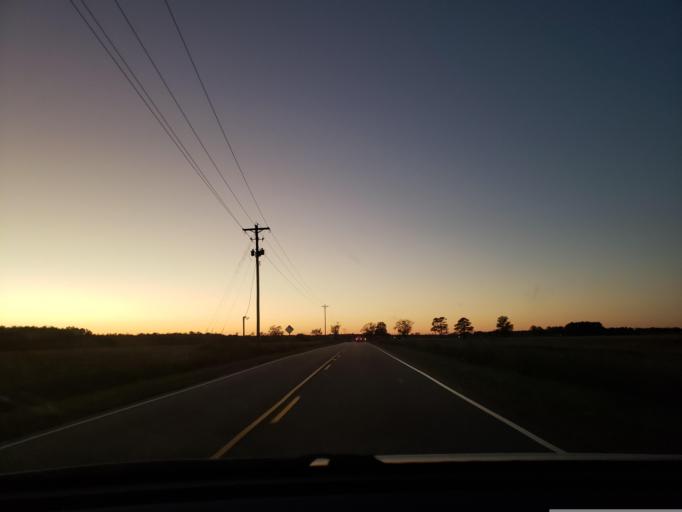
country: US
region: North Carolina
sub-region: Duplin County
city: Kenansville
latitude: 34.8866
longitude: -77.8979
